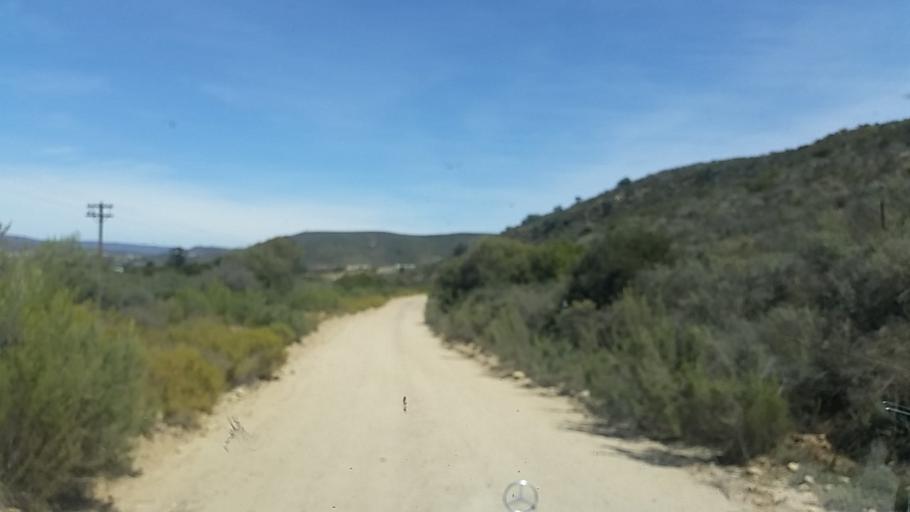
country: ZA
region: Western Cape
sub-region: Eden District Municipality
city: Knysna
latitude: -33.6388
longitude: 23.1485
